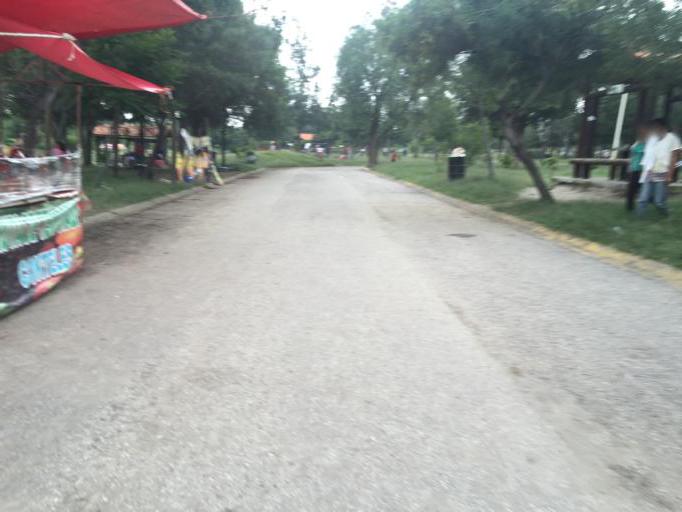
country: MX
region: Mexico
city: Cuautitlan Izcalli
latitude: 19.6526
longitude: -99.2230
